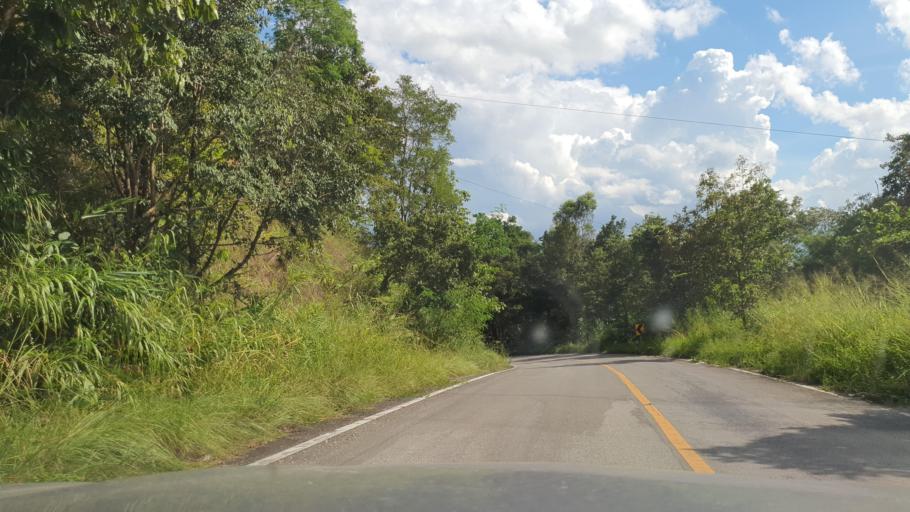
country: TH
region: Chiang Rai
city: Wiang Pa Pao
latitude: 19.3327
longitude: 99.4597
